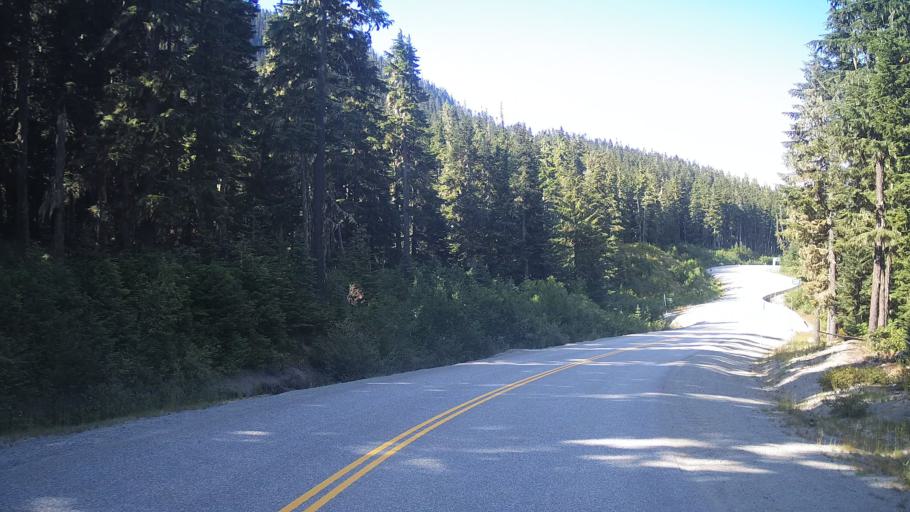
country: CA
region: British Columbia
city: Pemberton
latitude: 50.3683
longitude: -122.5034
